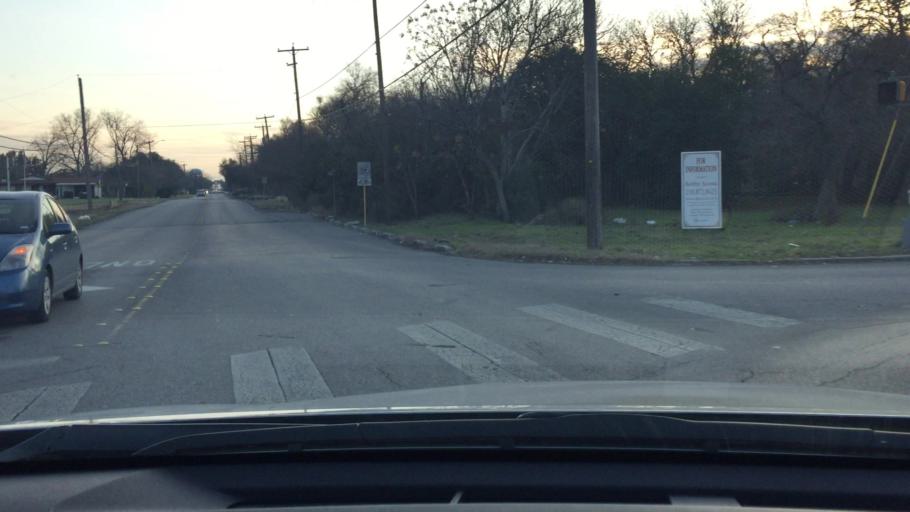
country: US
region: Texas
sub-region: Bexar County
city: Terrell Hills
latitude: 29.4958
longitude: -98.4244
